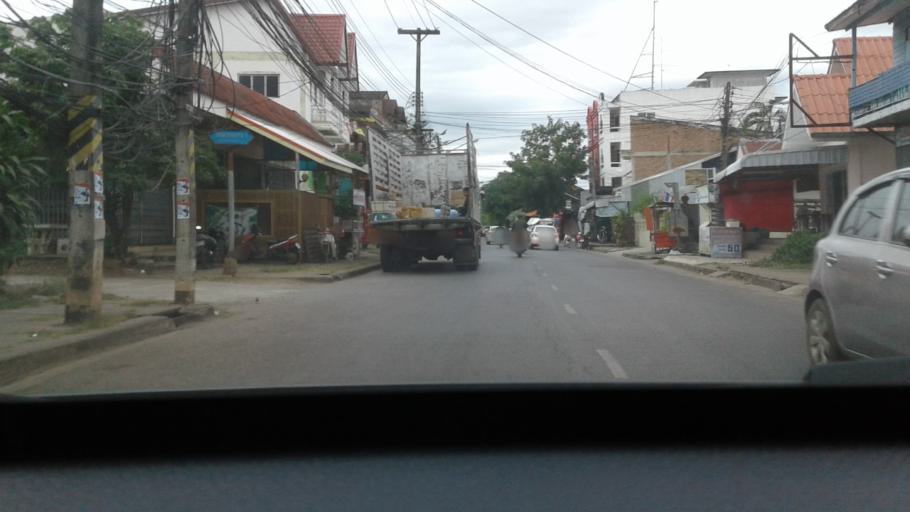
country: TH
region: Changwat Udon Thani
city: Udon Thani
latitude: 17.3989
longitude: 102.7822
